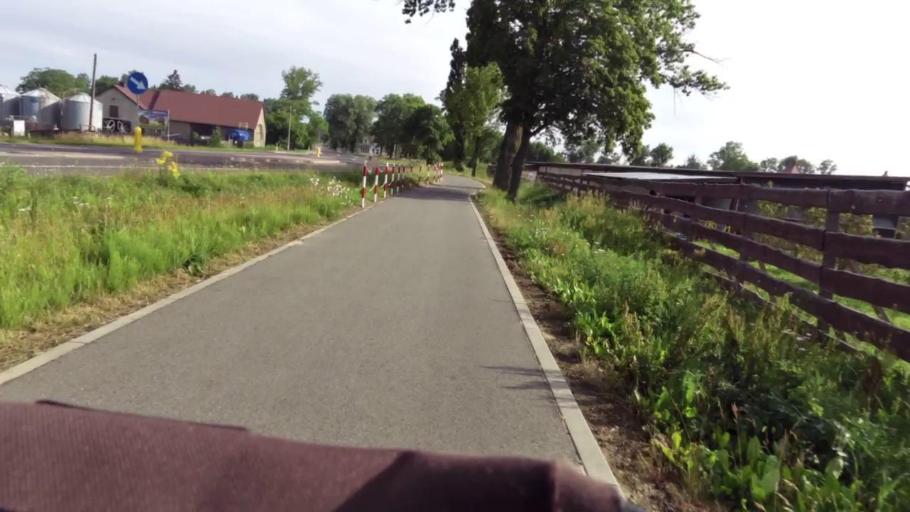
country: PL
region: West Pomeranian Voivodeship
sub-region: Powiat kamienski
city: Kamien Pomorski
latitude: 53.9959
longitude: 14.8175
